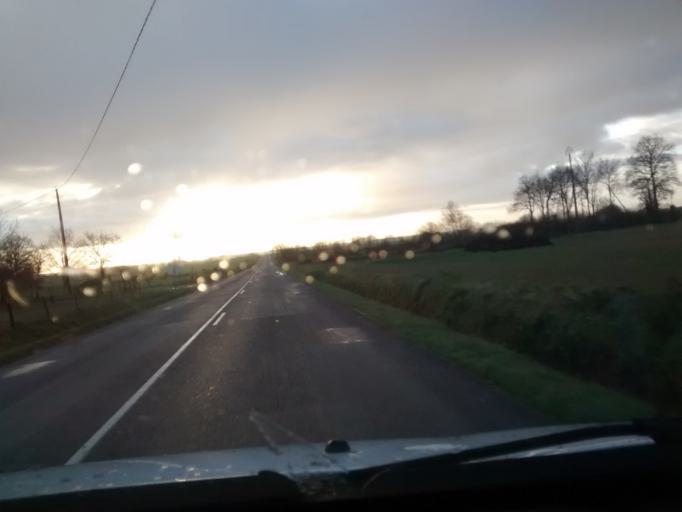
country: FR
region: Brittany
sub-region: Departement d'Ille-et-Vilaine
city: Bais
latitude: 47.9845
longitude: -1.2828
